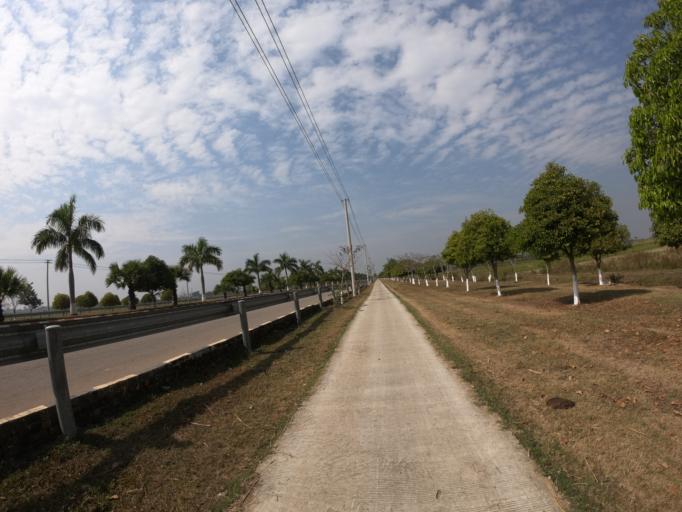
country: MM
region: Mandalay
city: Pyinmana
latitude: 19.6175
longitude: 96.1707
